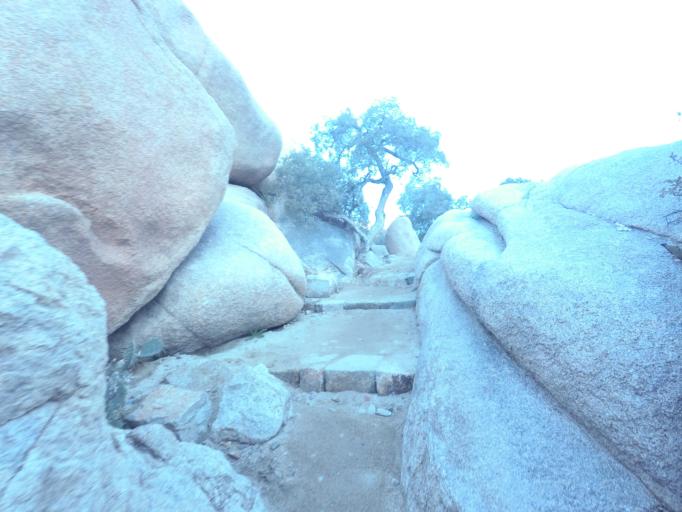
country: US
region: California
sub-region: San Bernardino County
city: Twentynine Palms
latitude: 34.0290
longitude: -116.1440
